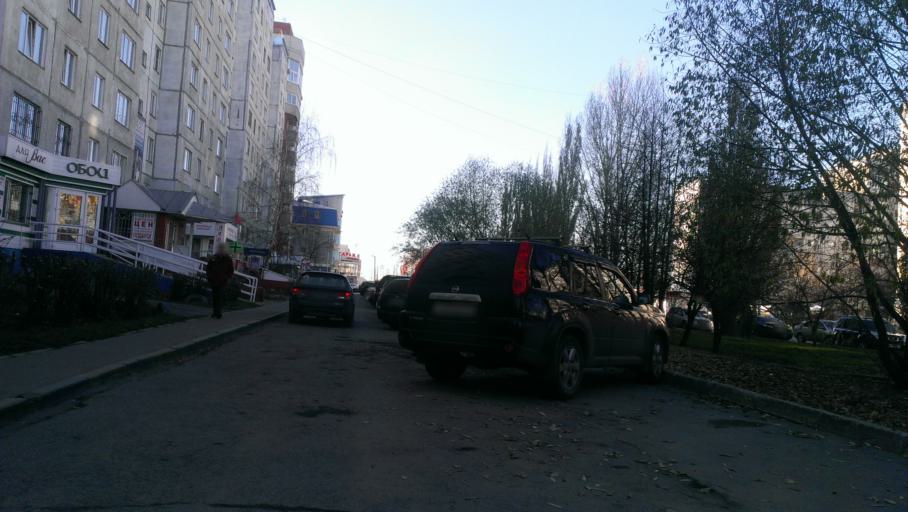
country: RU
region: Altai Krai
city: Novosilikatnyy
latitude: 53.3355
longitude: 83.6720
